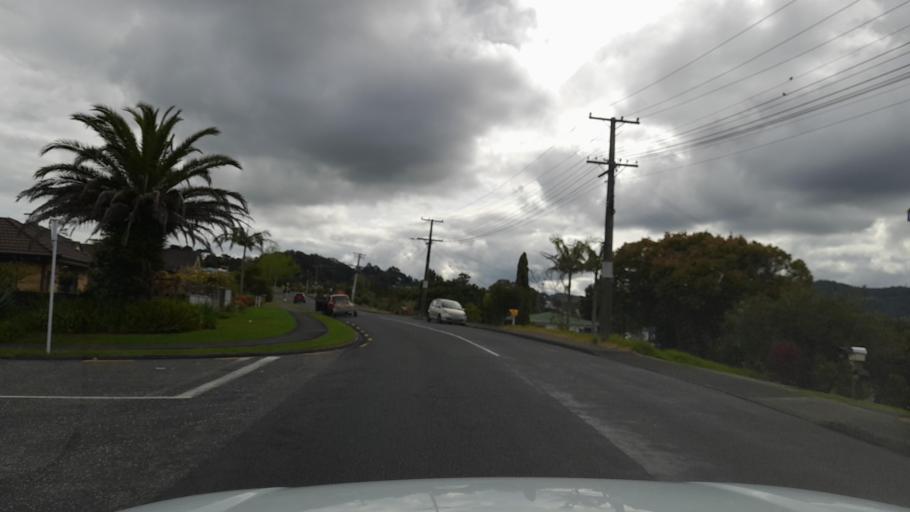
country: NZ
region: Northland
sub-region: Whangarei
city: Whangarei
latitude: -35.7380
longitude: 174.3250
